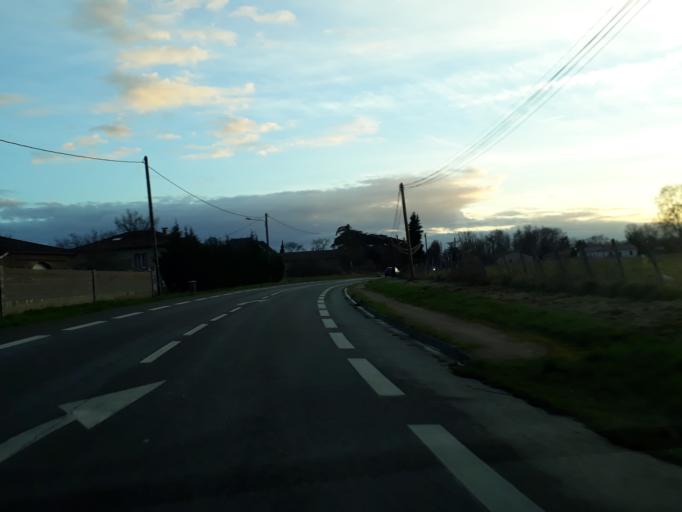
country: FR
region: Midi-Pyrenees
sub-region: Departement de la Haute-Garonne
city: Marquefave
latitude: 43.3223
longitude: 1.2451
